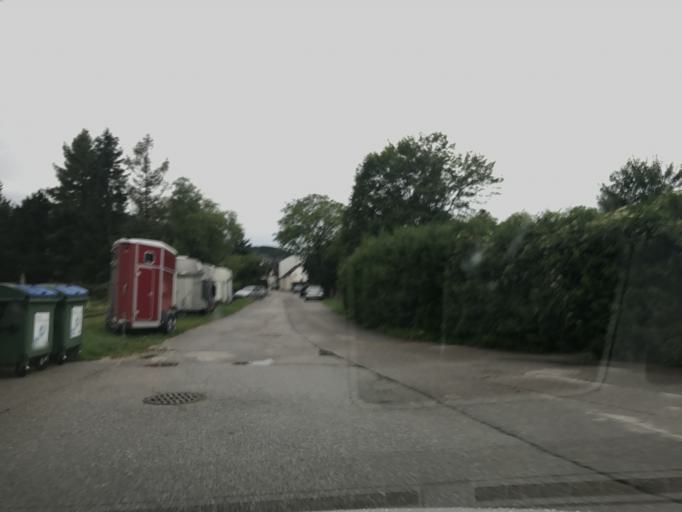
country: AT
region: Lower Austria
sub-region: Politischer Bezirk Wiener Neustadt
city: Markt Piesting
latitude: 47.8558
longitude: 16.1115
